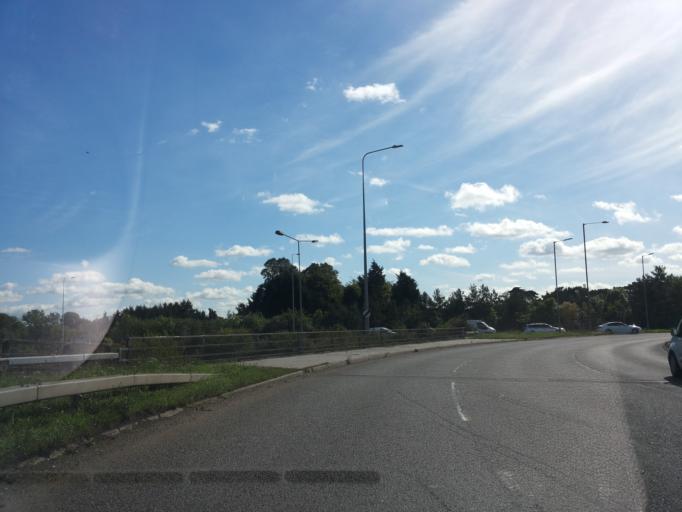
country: GB
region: England
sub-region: Kent
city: Boxley
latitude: 51.2883
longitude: 0.5528
